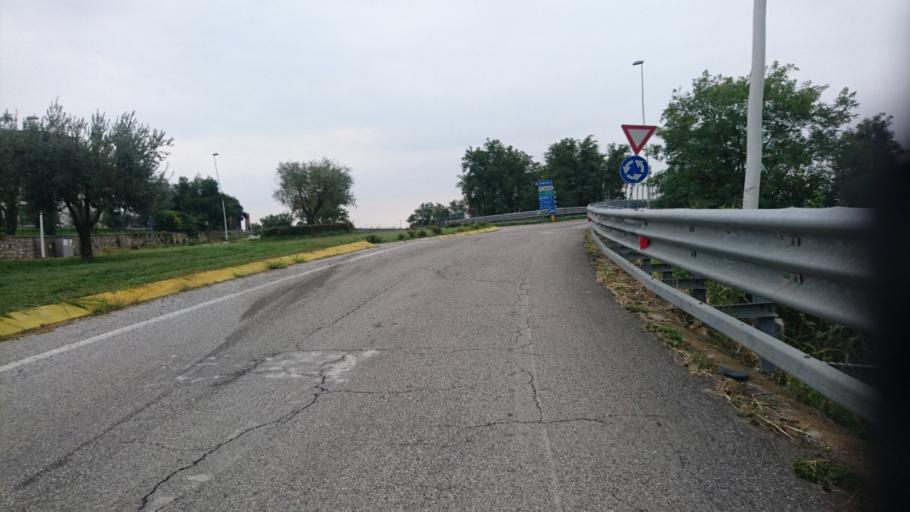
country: IT
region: Veneto
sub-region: Provincia di Verona
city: Soave
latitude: 45.4095
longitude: 11.2576
